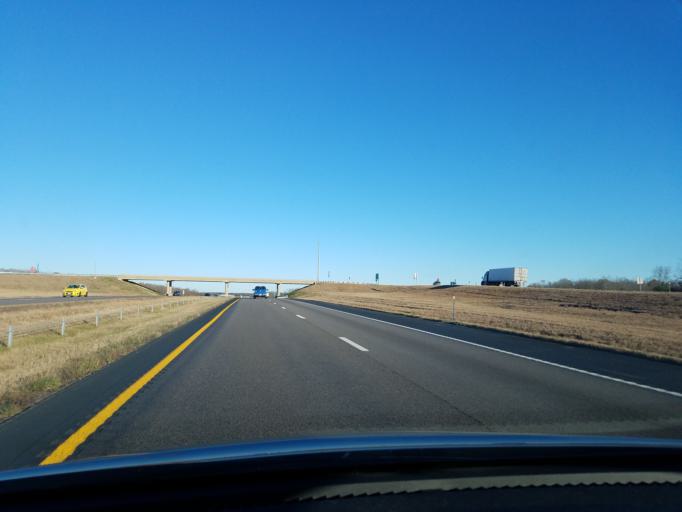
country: US
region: Missouri
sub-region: Crawford County
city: Cuba
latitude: 38.0441
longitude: -91.4892
